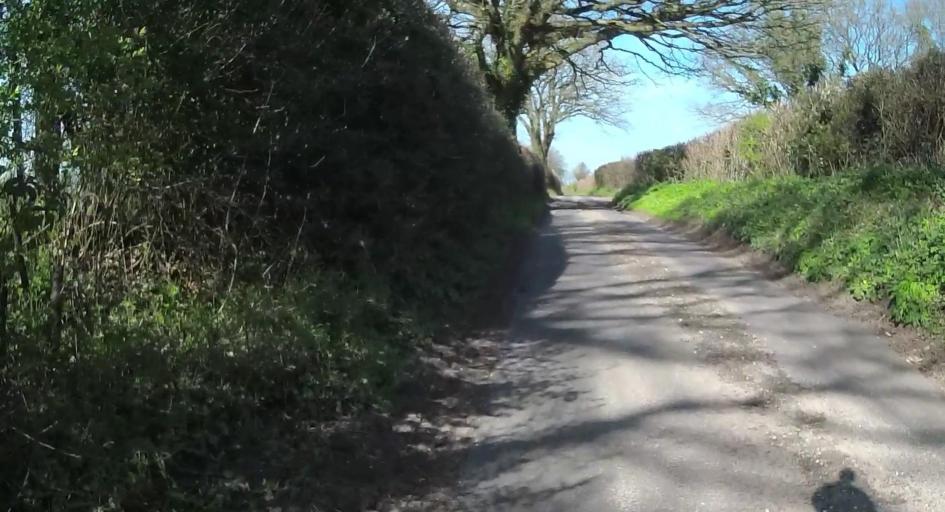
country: GB
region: England
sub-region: Hampshire
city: Highclere
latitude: 51.2778
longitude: -1.4095
